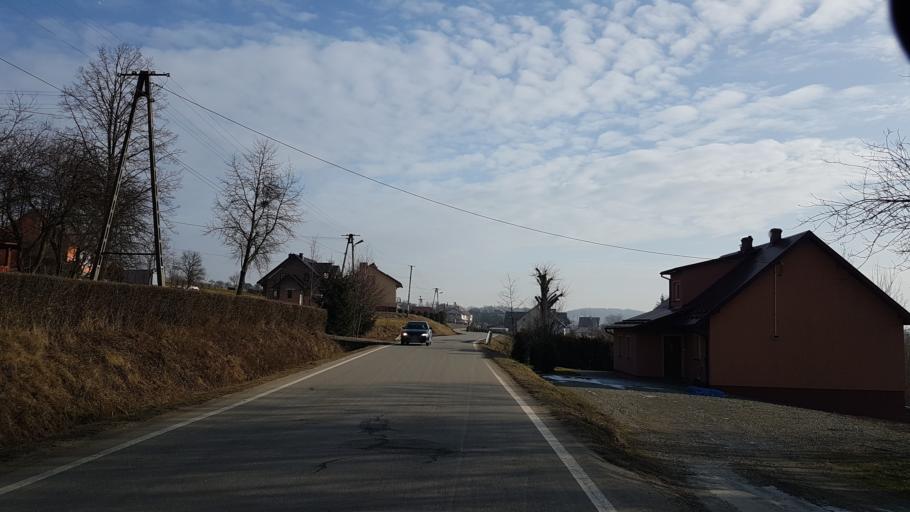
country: PL
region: Lesser Poland Voivodeship
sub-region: Powiat limanowski
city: Lukowica
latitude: 49.6310
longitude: 20.5390
